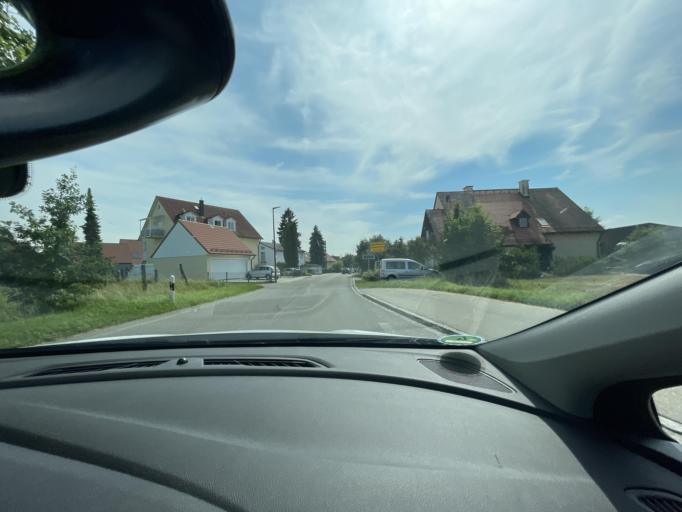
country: DE
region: Bavaria
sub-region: Upper Bavaria
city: Rohrmoos
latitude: 48.3243
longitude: 11.4155
